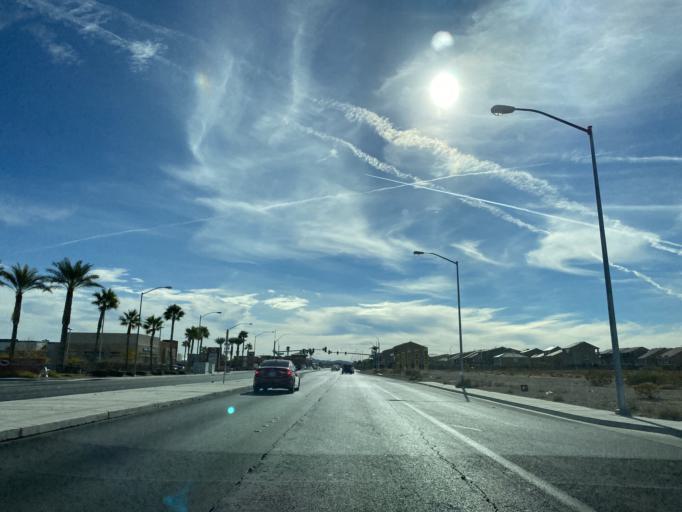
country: US
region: Nevada
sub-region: Clark County
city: Enterprise
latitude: 36.0639
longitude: -115.2247
